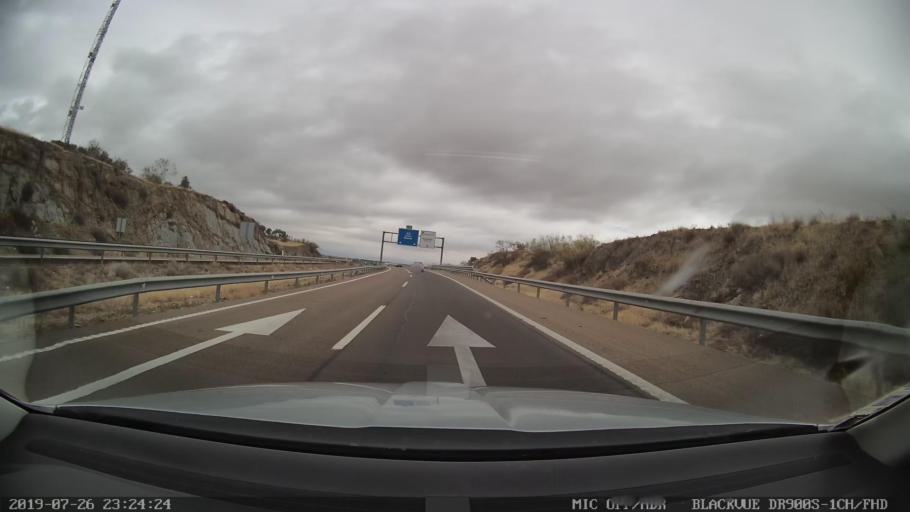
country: ES
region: Extremadura
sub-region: Provincia de Caceres
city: Escurial
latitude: 39.1709
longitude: -5.9008
